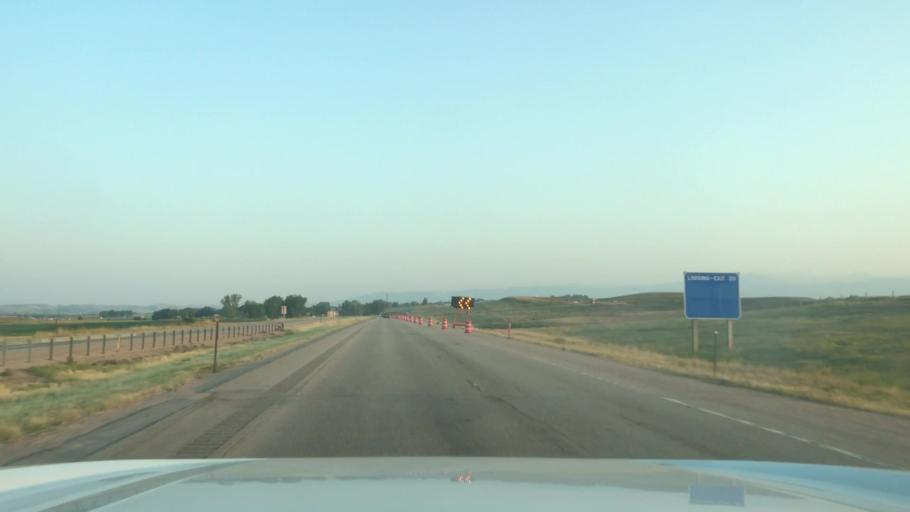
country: US
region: Wyoming
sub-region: Sheridan County
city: Sheridan
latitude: 44.8571
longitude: -106.9899
